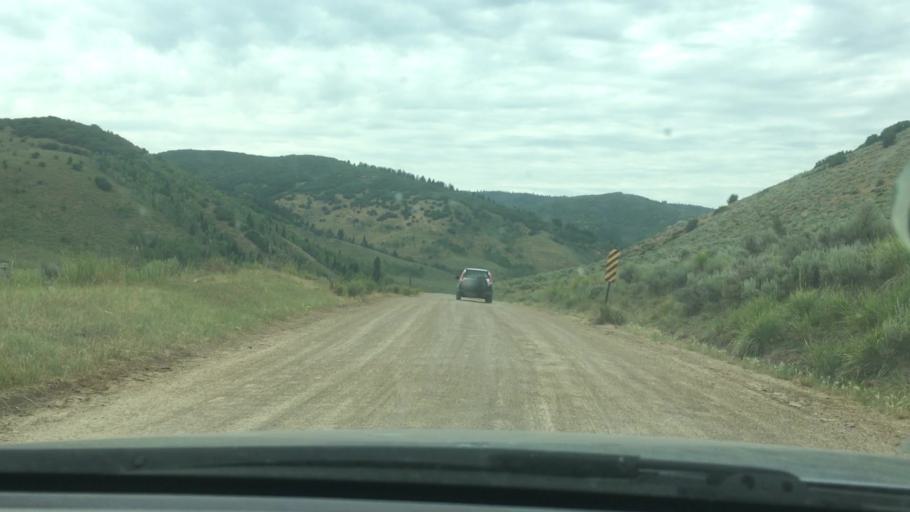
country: US
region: Utah
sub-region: Summit County
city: Summit Park
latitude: 40.7807
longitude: -111.5887
